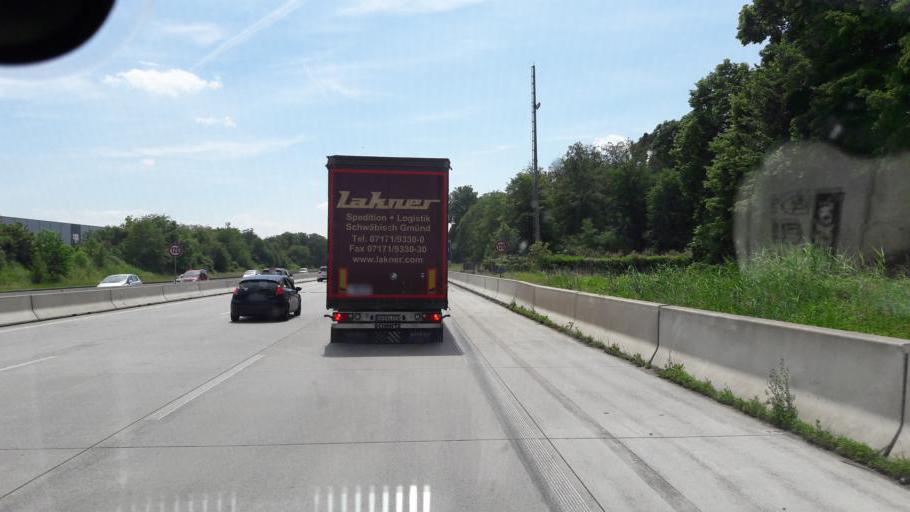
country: DE
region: Baden-Wuerttemberg
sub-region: Karlsruhe Region
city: Forst
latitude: 49.1677
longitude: 8.5720
